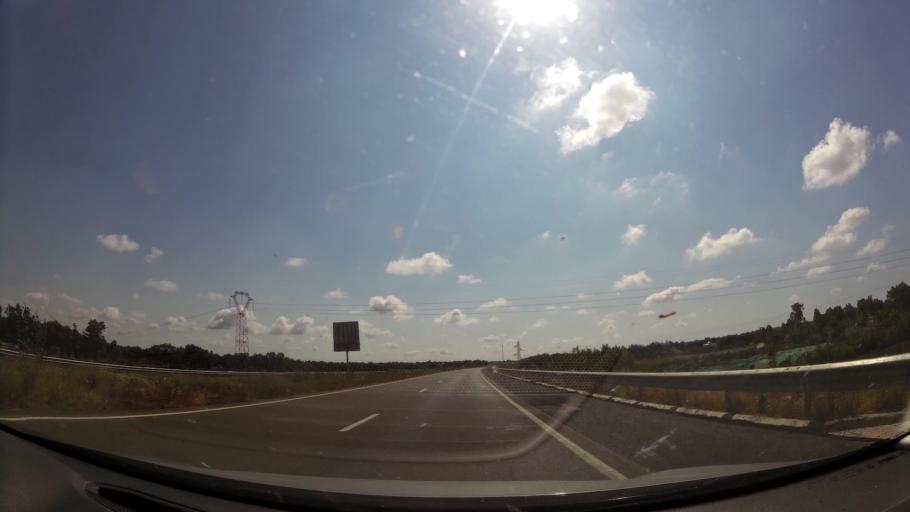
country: MA
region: Rabat-Sale-Zemmour-Zaer
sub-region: Skhirate-Temara
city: Temara
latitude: 33.8420
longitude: -6.8510
